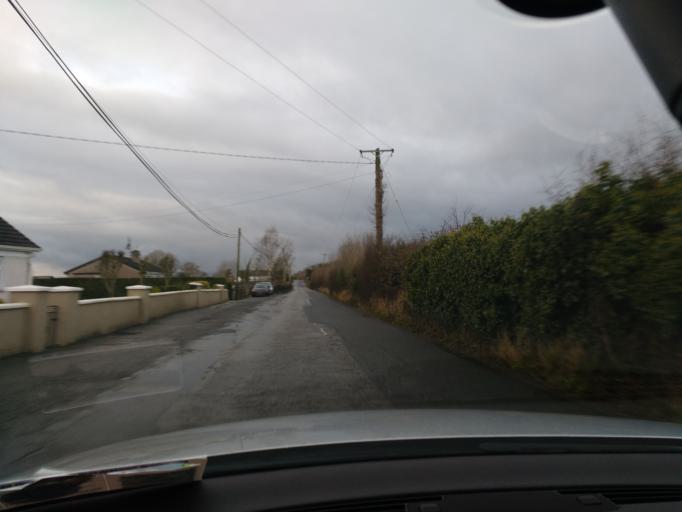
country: IE
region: Munster
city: Thurles
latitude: 52.6371
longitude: -7.8514
